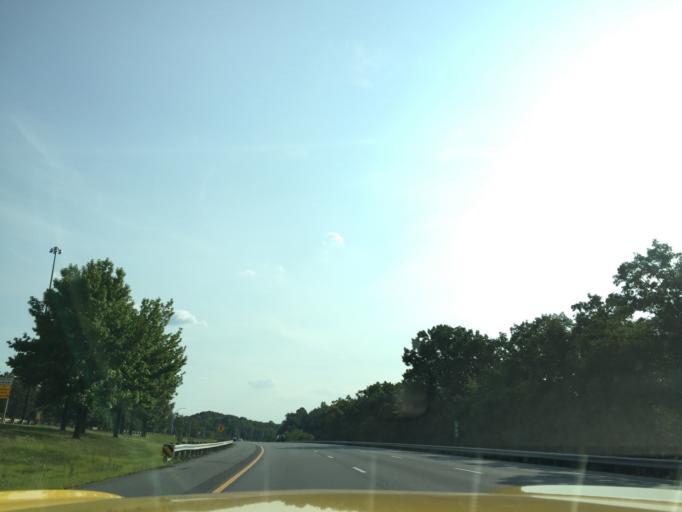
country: US
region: Maryland
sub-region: Cecil County
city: Charlestown
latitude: 39.6124
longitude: -76.0106
